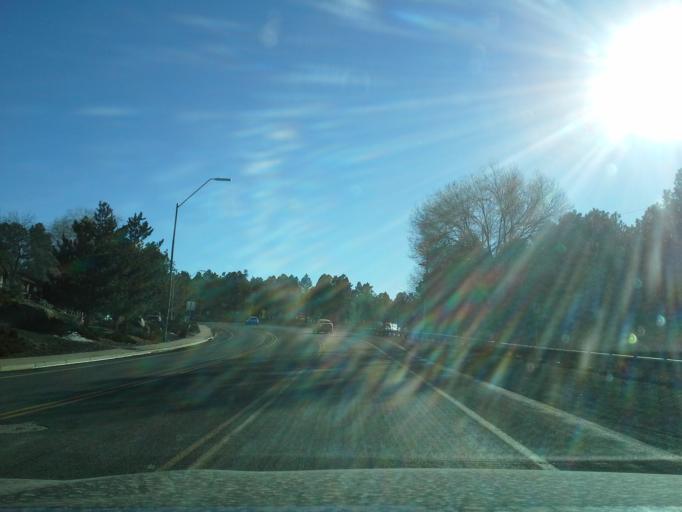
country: US
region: Arizona
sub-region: Coconino County
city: Flagstaff
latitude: 35.1854
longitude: -111.6478
